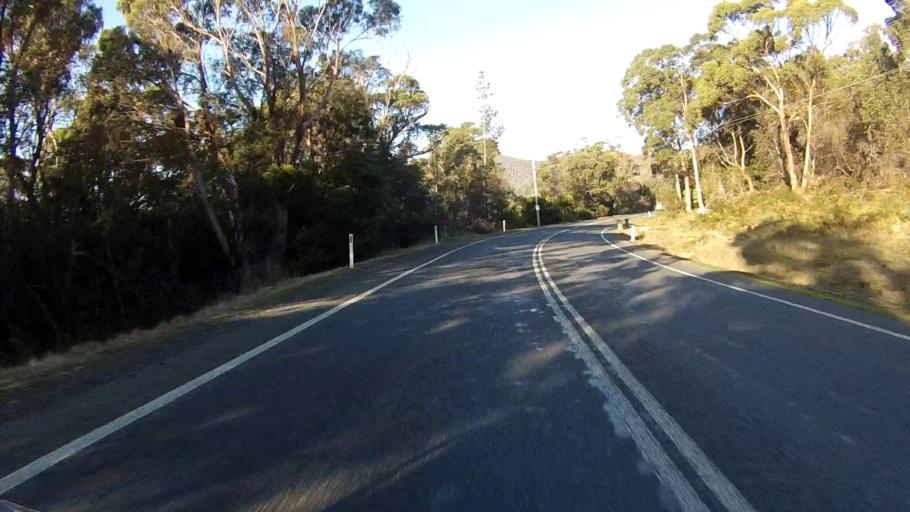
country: AU
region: Tasmania
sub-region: Clarence
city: Sandford
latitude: -43.0233
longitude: 147.8749
